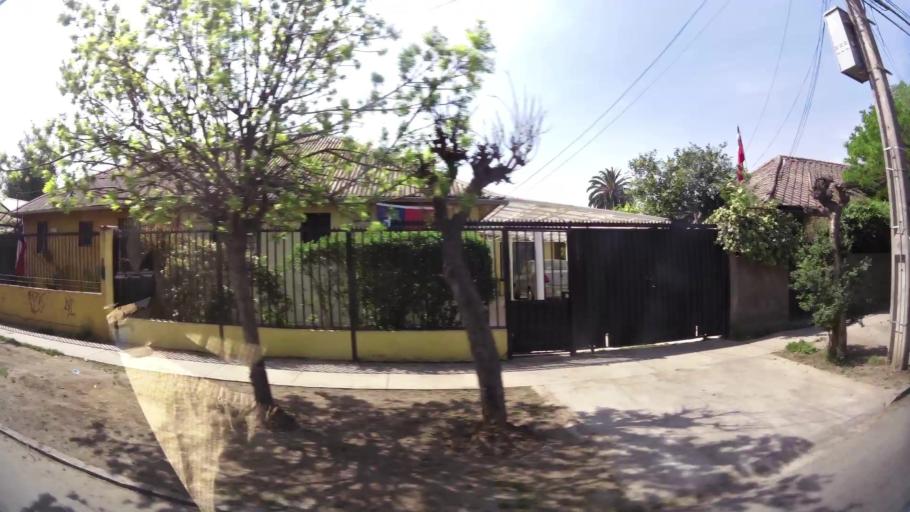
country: CL
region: Santiago Metropolitan
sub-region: Provincia de Santiago
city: Lo Prado
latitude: -33.4169
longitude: -70.6962
